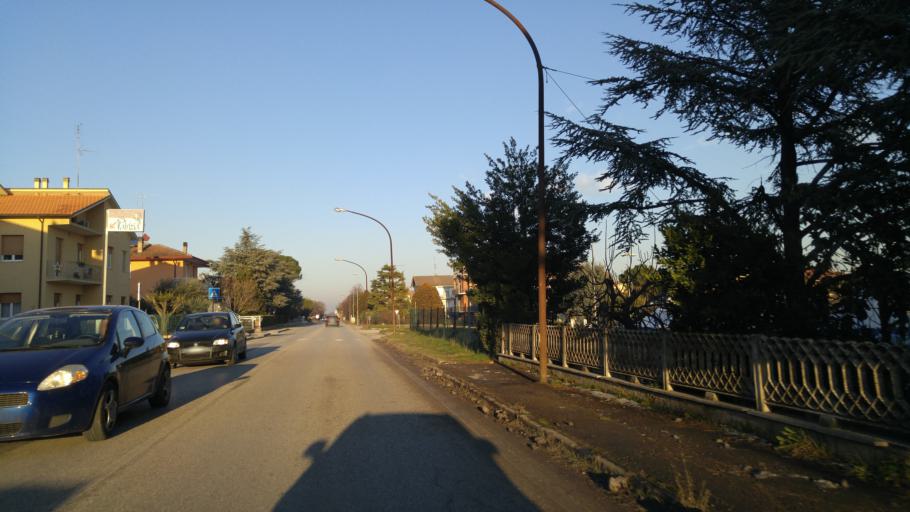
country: IT
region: The Marches
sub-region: Provincia di Pesaro e Urbino
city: Monte Porzio
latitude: 43.6991
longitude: 13.0611
